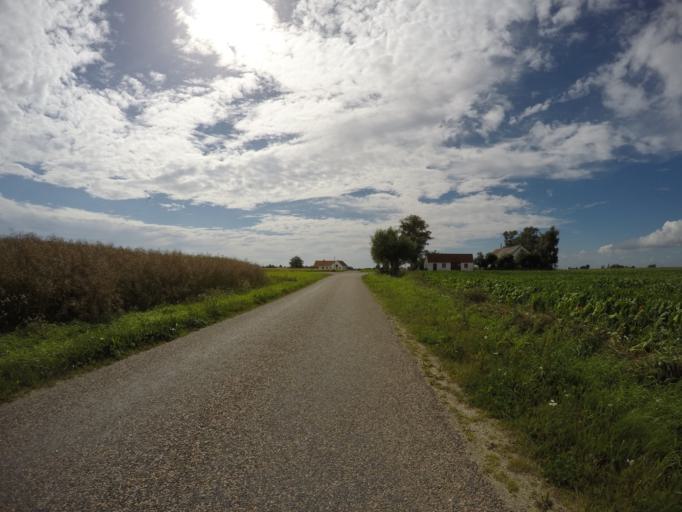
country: SE
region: Skane
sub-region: Ystads Kommun
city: Kopingebro
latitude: 55.4138
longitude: 14.1526
